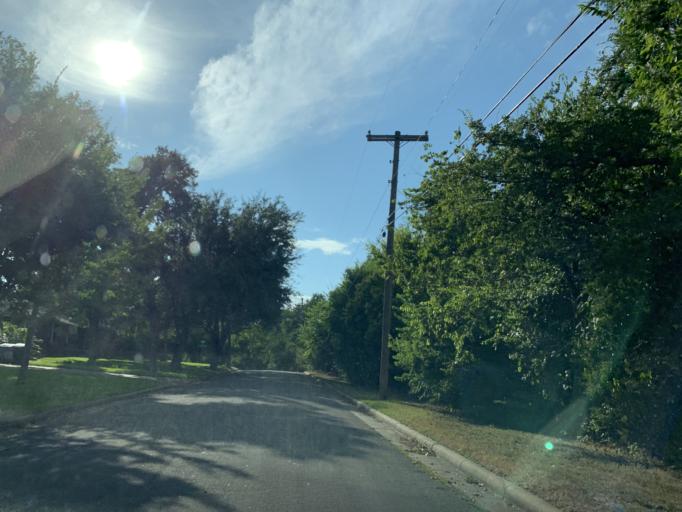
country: US
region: Texas
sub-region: Dallas County
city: Dallas
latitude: 32.7337
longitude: -96.8315
